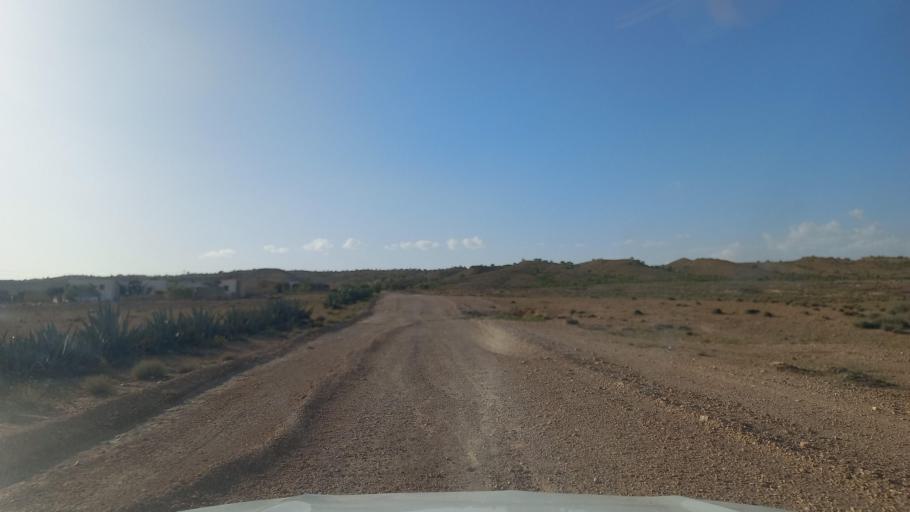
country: TN
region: Al Qasrayn
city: Sbiba
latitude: 35.3637
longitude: 9.0003
